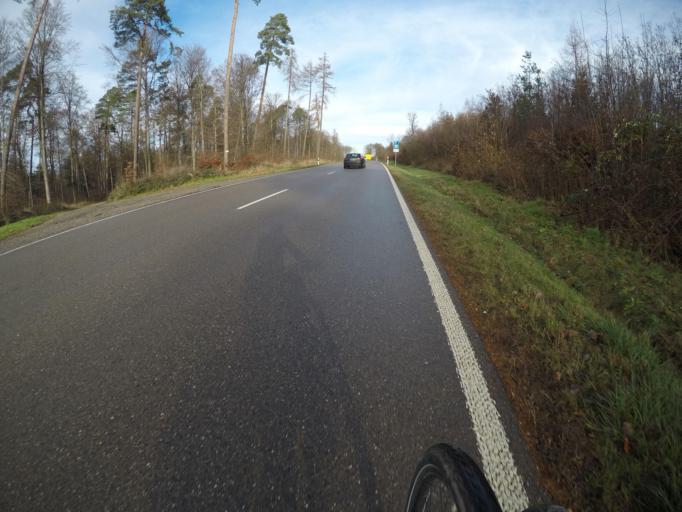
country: DE
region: Baden-Wuerttemberg
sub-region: Regierungsbezirk Stuttgart
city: Winterbach
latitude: 48.7735
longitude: 9.4588
